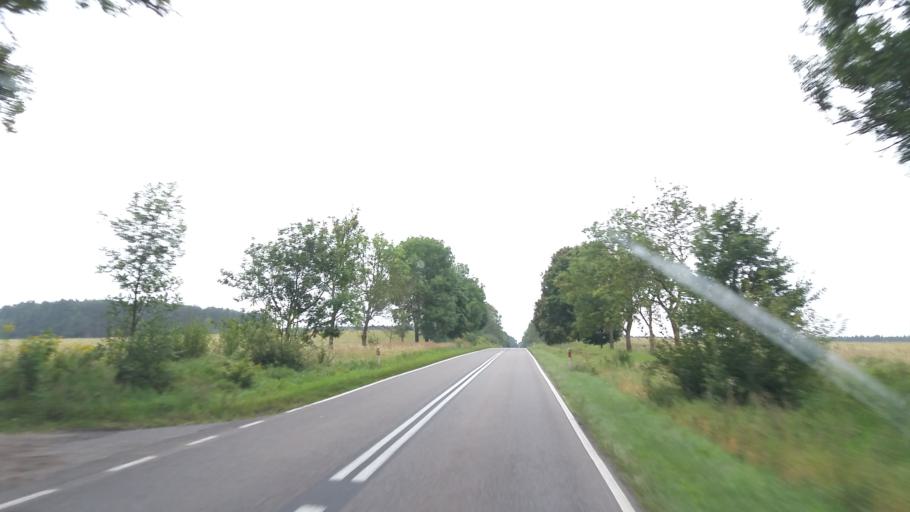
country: PL
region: West Pomeranian Voivodeship
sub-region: Powiat mysliborski
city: Barlinek
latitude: 53.0116
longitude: 15.2614
